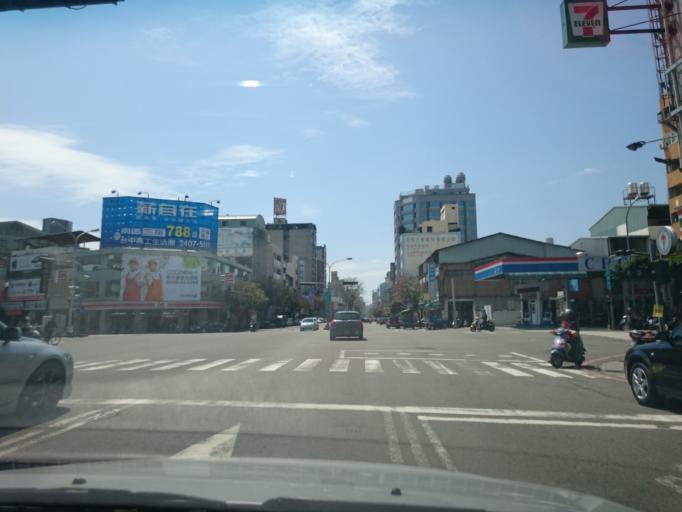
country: TW
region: Taiwan
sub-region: Taichung City
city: Taichung
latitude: 24.1319
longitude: 120.6906
